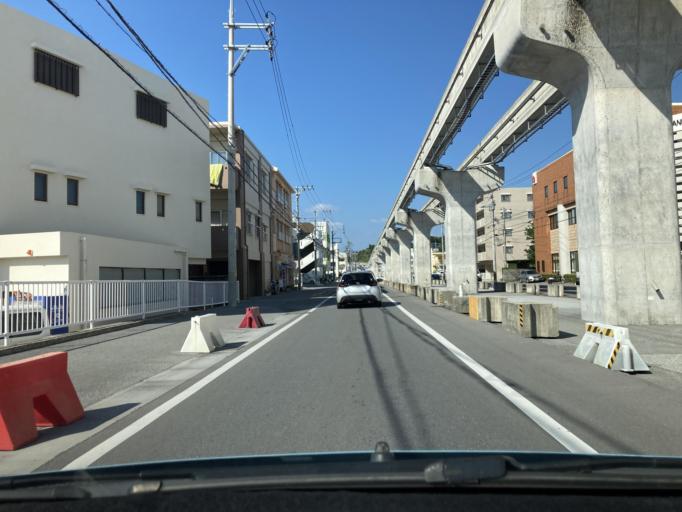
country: JP
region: Okinawa
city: Ginowan
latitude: 26.2300
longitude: 127.7290
